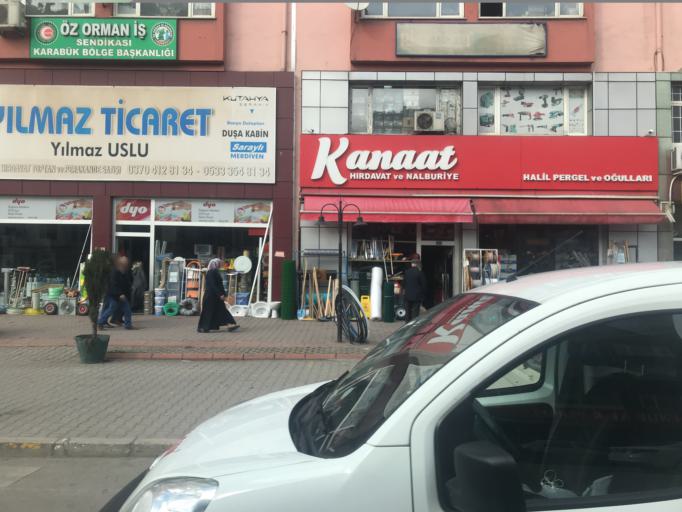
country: TR
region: Karabuk
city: Karabuk
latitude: 41.1941
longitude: 32.6141
